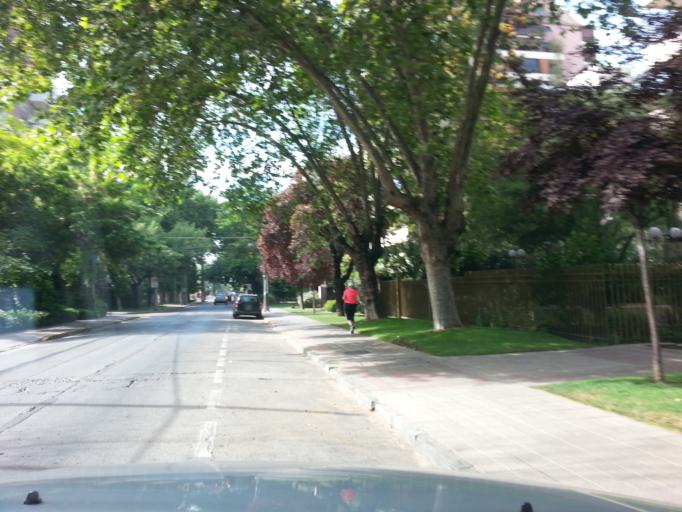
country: CL
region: Santiago Metropolitan
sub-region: Provincia de Santiago
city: Villa Presidente Frei, Nunoa, Santiago, Chile
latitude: -33.4318
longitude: -70.5967
